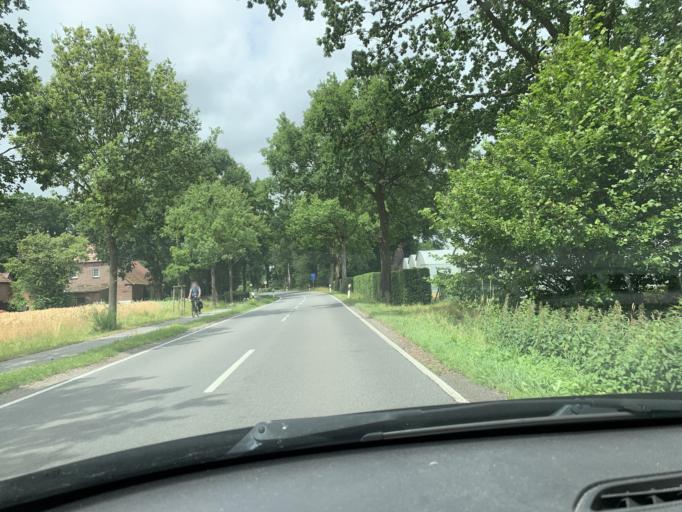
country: DE
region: Lower Saxony
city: Wiefelstede
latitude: 53.2053
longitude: 8.1161
